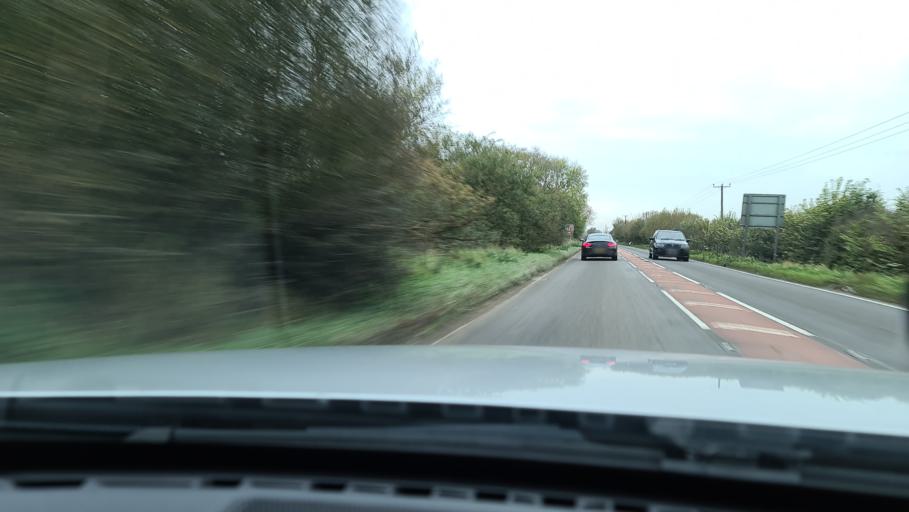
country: GB
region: England
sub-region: Buckinghamshire
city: Steeple Claydon
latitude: 51.8732
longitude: -1.0536
